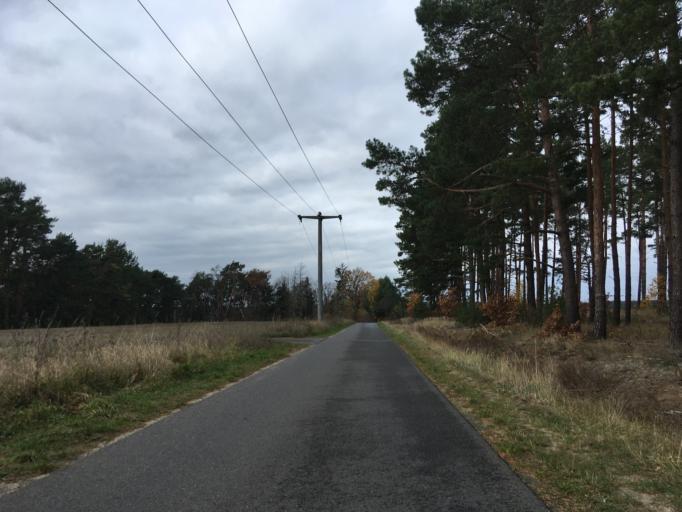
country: DE
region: Brandenburg
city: Jamlitz
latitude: 52.0854
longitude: 14.4401
